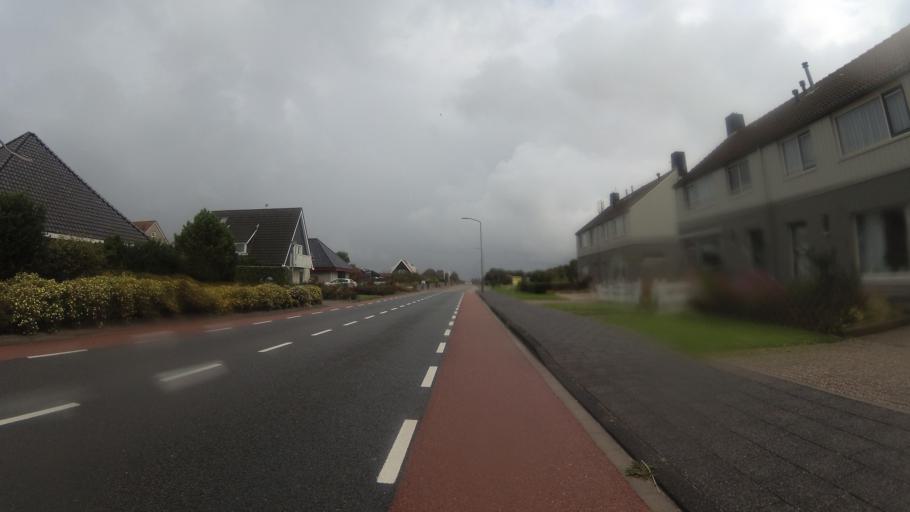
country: NL
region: North Holland
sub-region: Gemeente Schagen
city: Schagen
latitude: 52.8408
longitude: 4.6978
